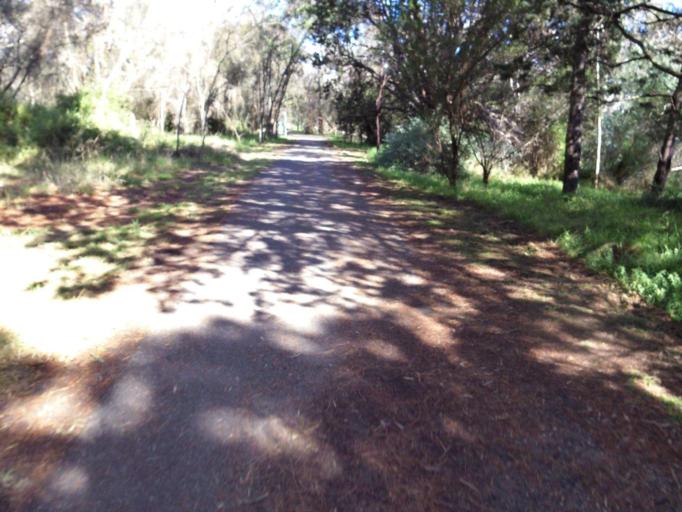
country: AU
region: Victoria
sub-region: Greater Geelong
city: Wandana Heights
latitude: -38.1482
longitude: 144.3120
